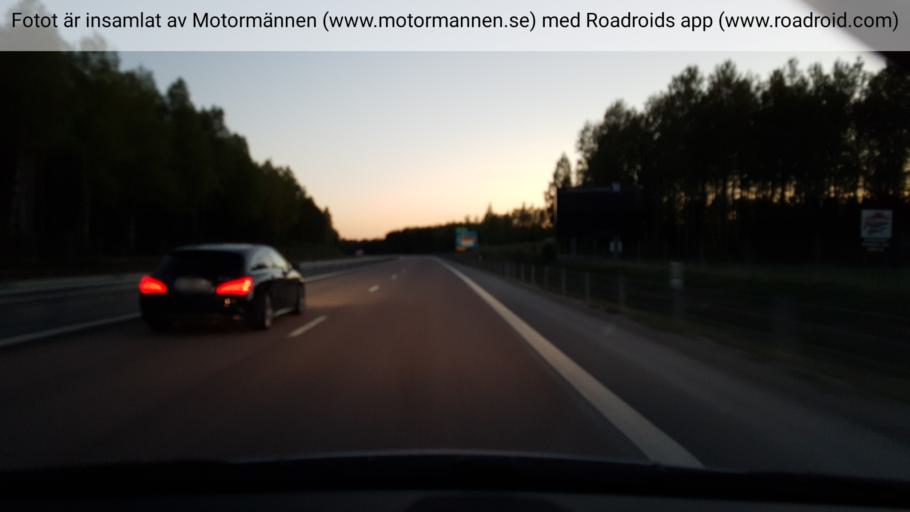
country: SE
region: Vaestmanland
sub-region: Vasteras
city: Tillberga
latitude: 59.6243
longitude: 16.6825
